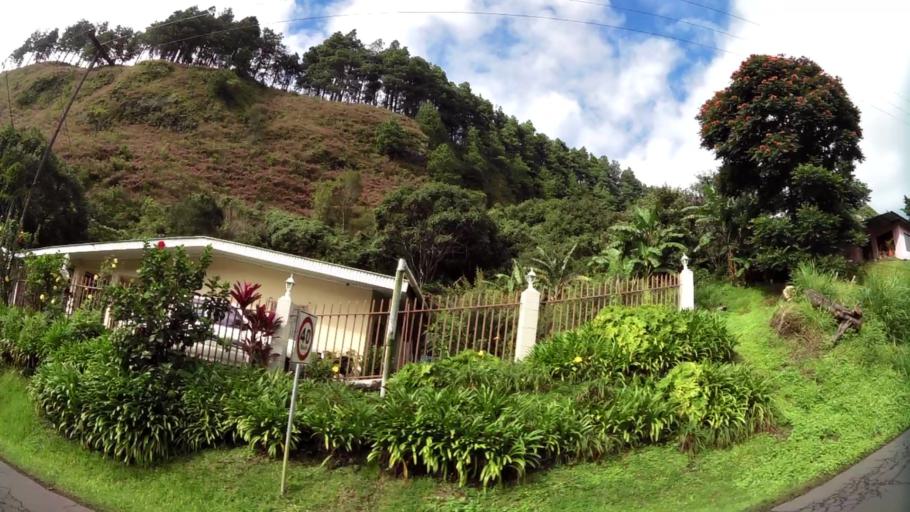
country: PA
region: Chiriqui
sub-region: Distrito Boquete
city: Boquete
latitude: 8.7848
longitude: -82.4351
